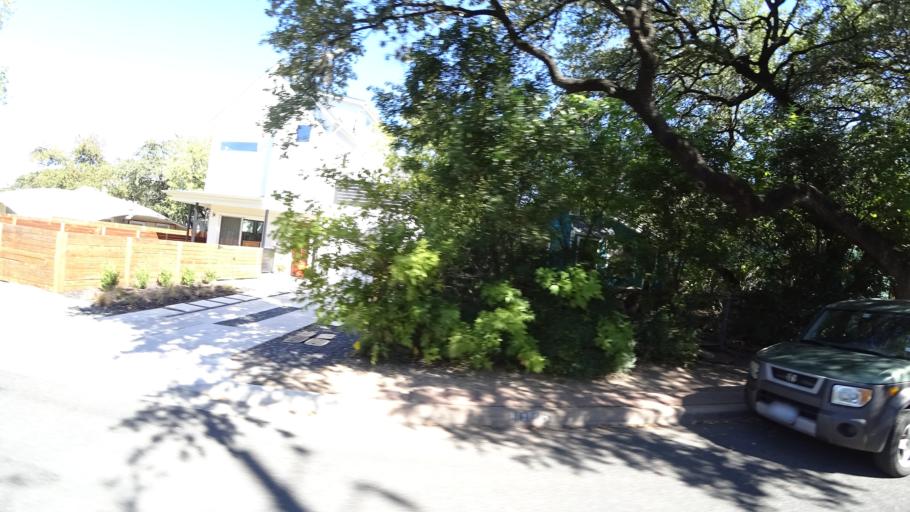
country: US
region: Texas
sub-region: Travis County
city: Austin
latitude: 30.2470
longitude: -97.7637
